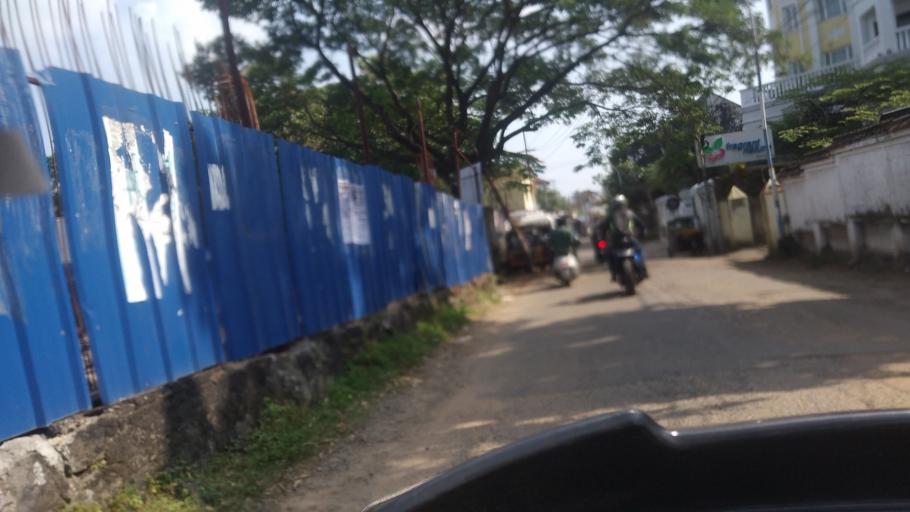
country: IN
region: Kerala
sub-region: Ernakulam
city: Cochin
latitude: 9.9675
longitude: 76.2524
